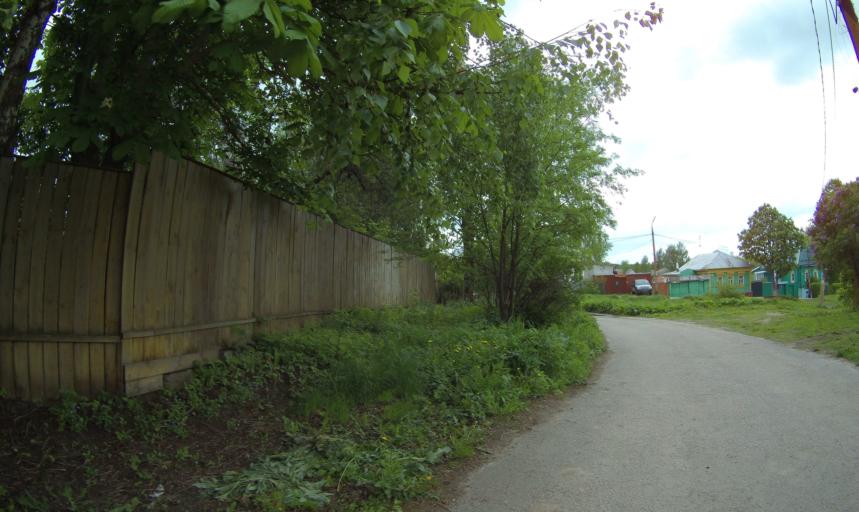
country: RU
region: Moskovskaya
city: Raduzhnyy
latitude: 55.1014
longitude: 38.7440
